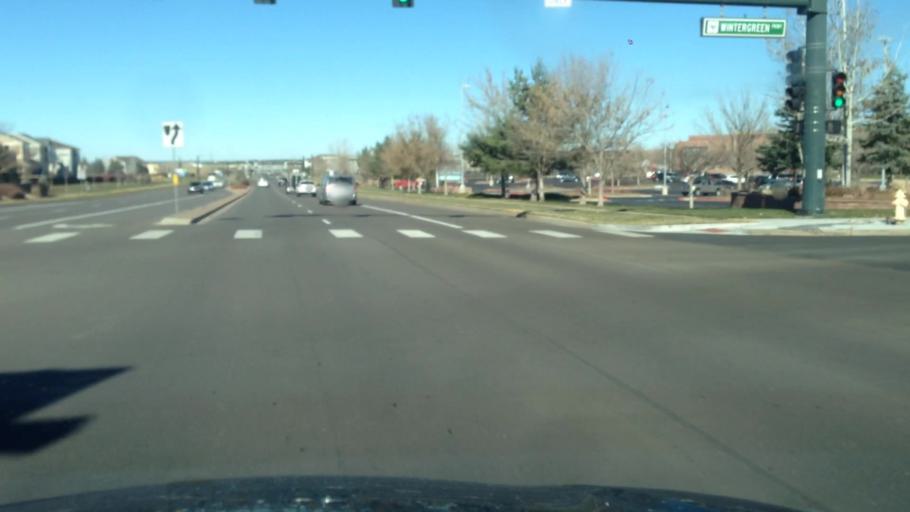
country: US
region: Colorado
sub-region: Douglas County
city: Stonegate
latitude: 39.5397
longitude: -104.7934
